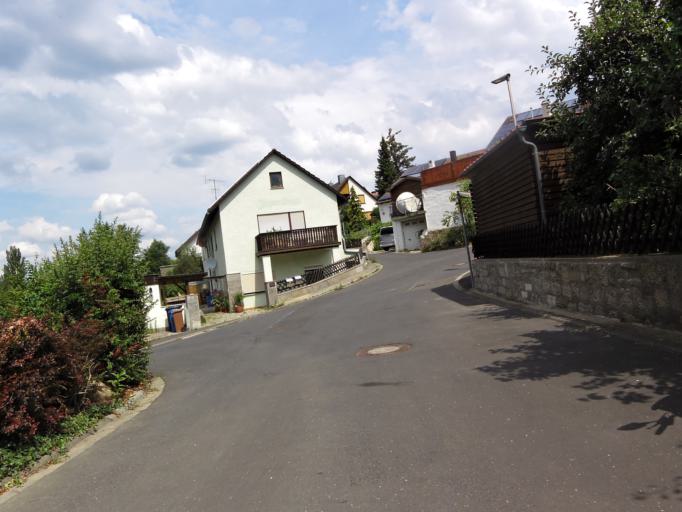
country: DE
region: Bavaria
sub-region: Regierungsbezirk Unterfranken
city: Eibelstadt
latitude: 49.7173
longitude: 9.9625
